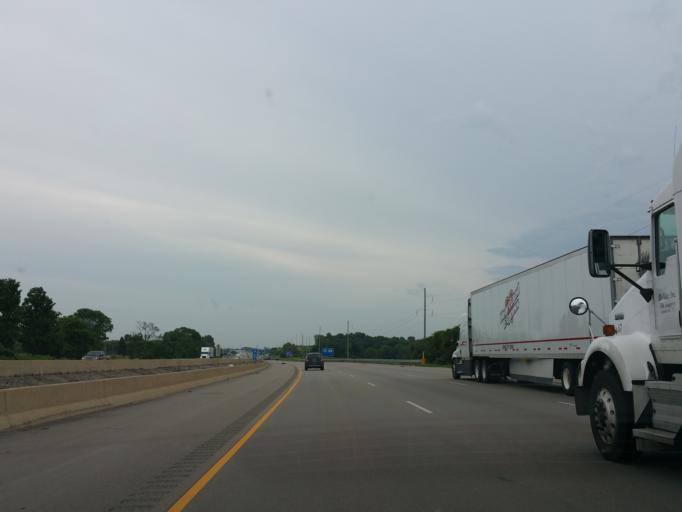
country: US
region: Wisconsin
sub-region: Dane County
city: Windsor
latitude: 43.2086
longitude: -89.3580
